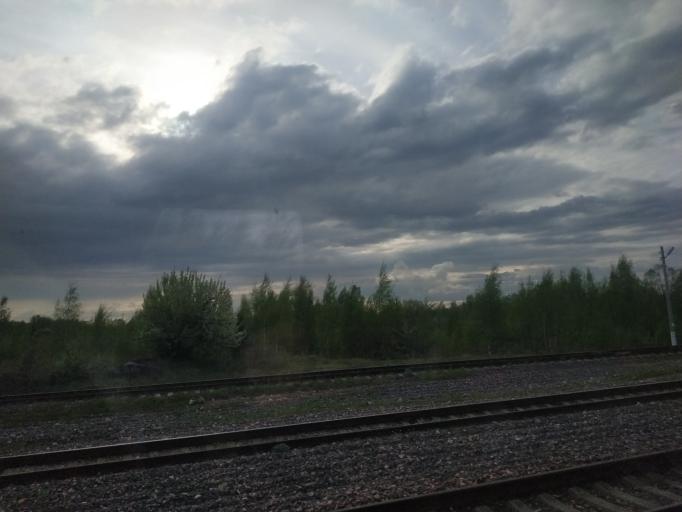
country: RU
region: Smolensk
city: Ugra
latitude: 54.7751
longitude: 34.3426
